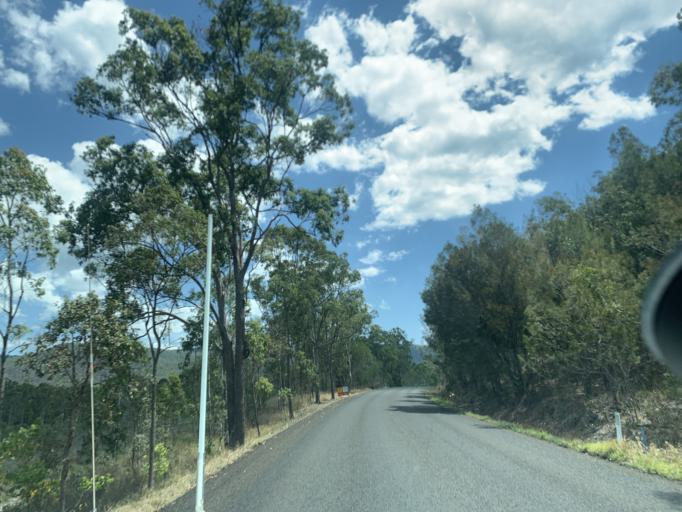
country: AU
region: Queensland
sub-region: Tablelands
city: Atherton
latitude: -17.3105
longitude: 145.4561
